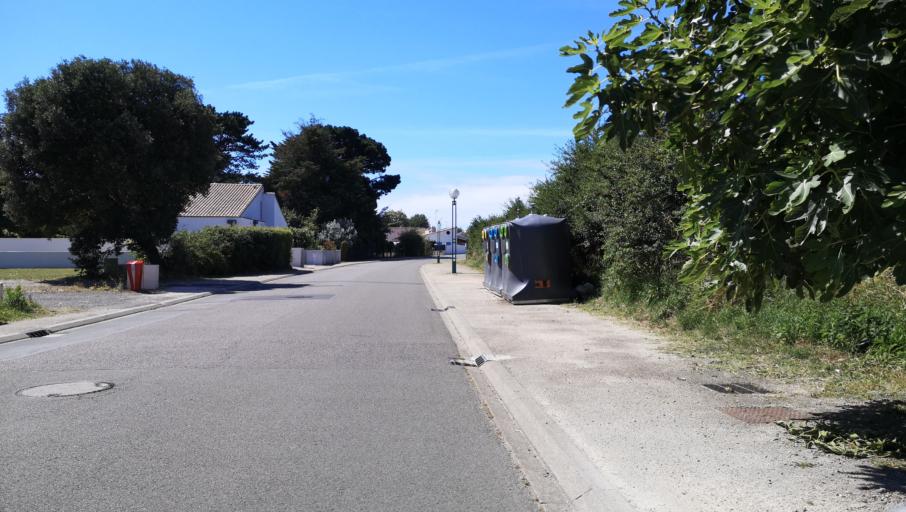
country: FR
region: Pays de la Loire
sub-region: Departement de la Vendee
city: Chateau-d'Olonne
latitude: 46.4790
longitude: -1.7499
